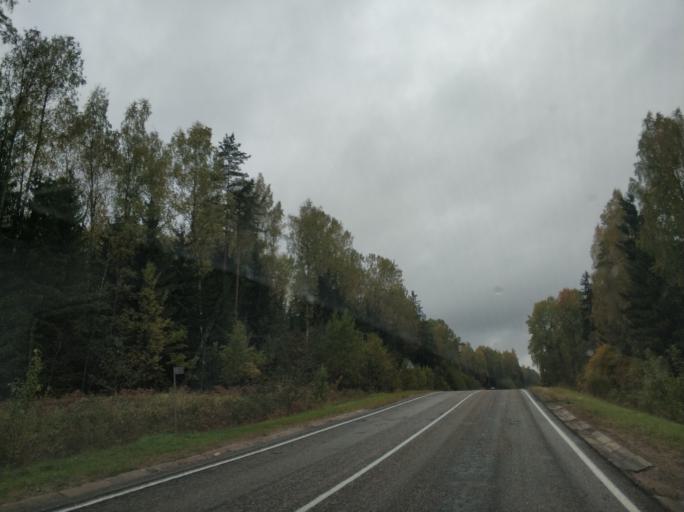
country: RU
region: Pskov
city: Opochka
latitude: 56.5184
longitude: 28.6594
